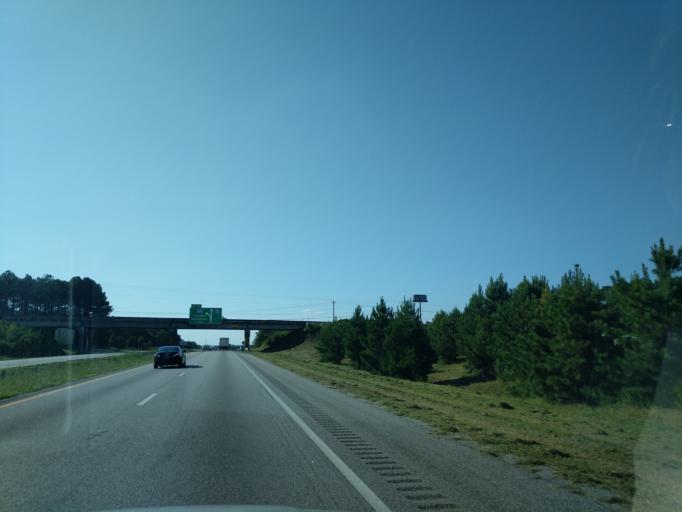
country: US
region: South Carolina
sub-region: Laurens County
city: Clinton
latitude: 34.5060
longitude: -81.8584
